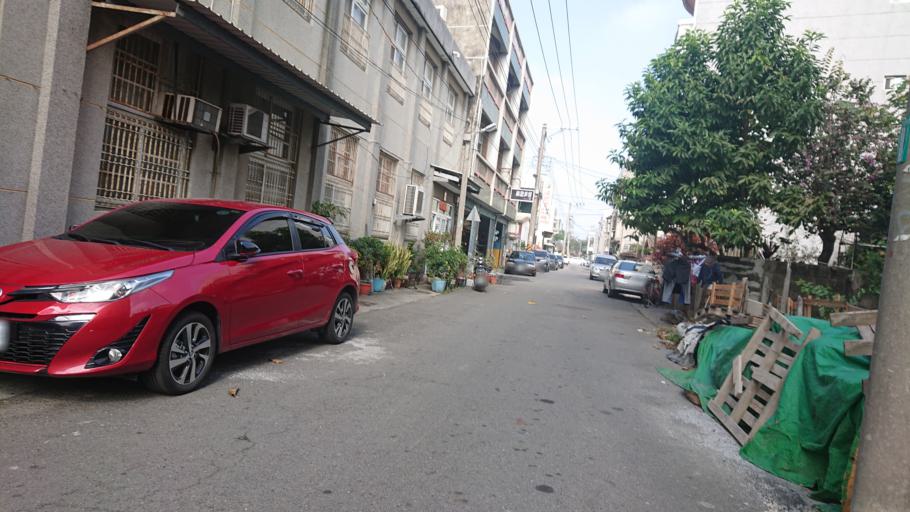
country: TW
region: Taiwan
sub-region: Chiayi
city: Taibao
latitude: 23.4685
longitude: 120.2436
